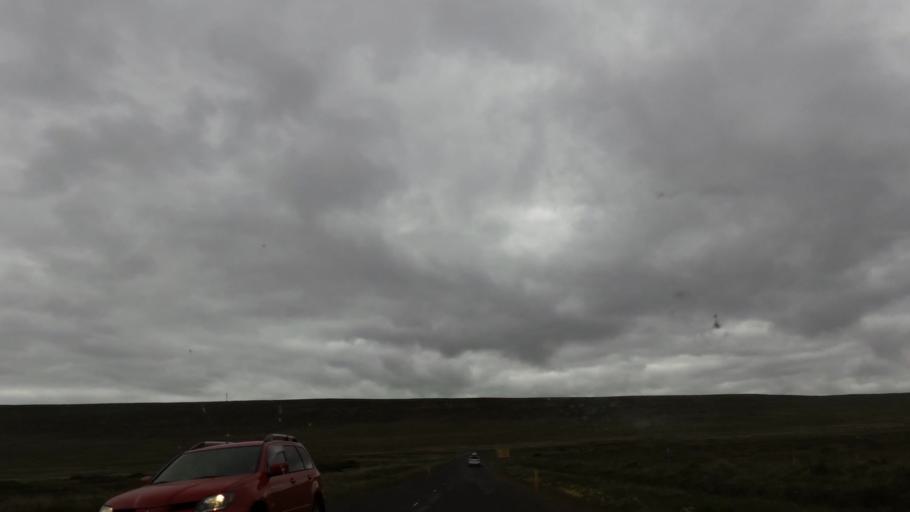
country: IS
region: West
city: Borgarnes
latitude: 65.0926
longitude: -21.7469
